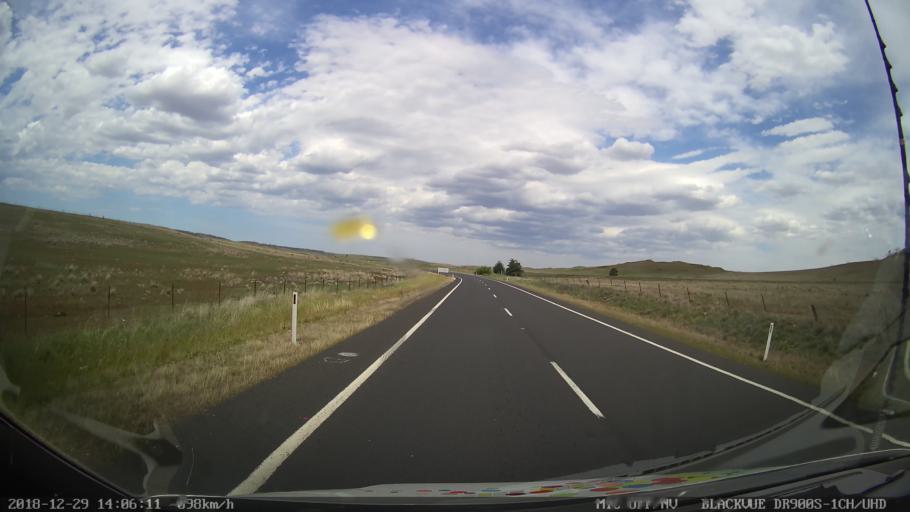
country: AU
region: New South Wales
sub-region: Cooma-Monaro
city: Cooma
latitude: -36.3403
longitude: 149.1983
